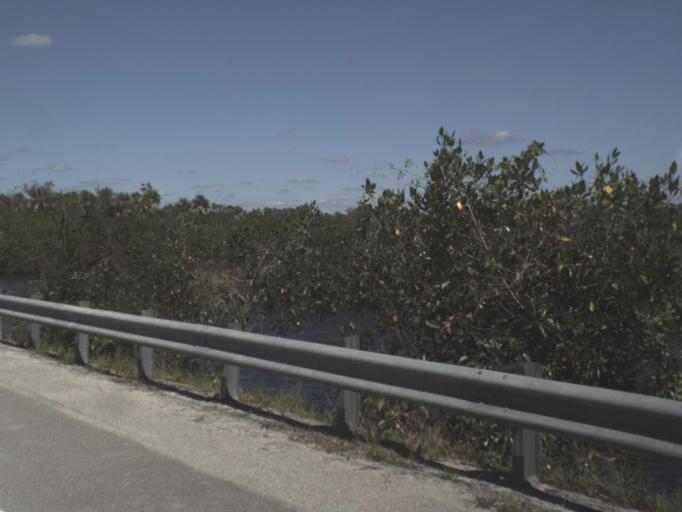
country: US
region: Florida
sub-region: Collier County
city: Marco
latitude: 25.9802
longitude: -81.5609
